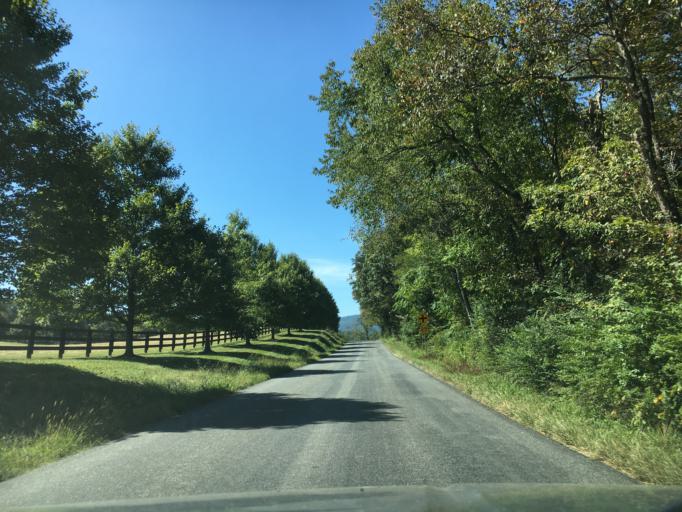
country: US
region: Virginia
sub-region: Albemarle County
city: Crozet
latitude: 38.0170
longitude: -78.7661
